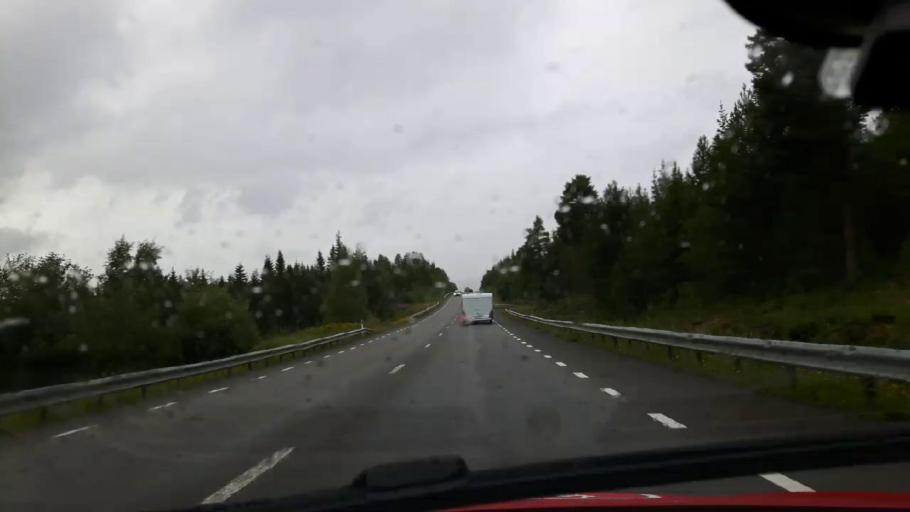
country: SE
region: Jaemtland
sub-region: Are Kommun
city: Jarpen
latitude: 63.3200
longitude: 13.5578
